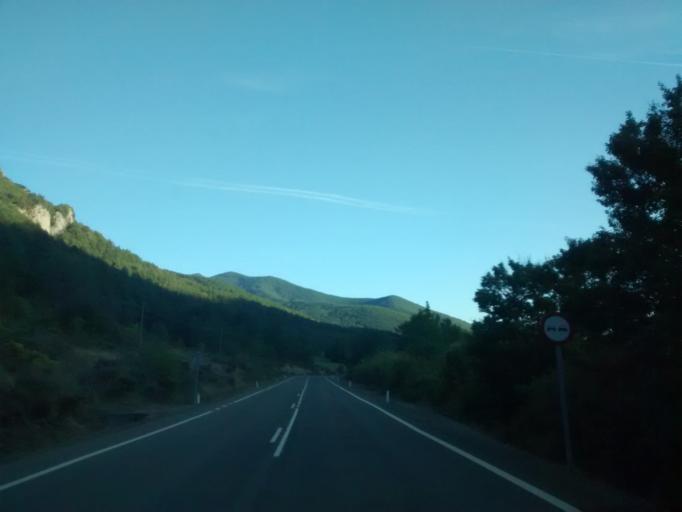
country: ES
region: Aragon
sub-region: Provincia de Huesca
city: Aragues del Puerto
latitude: 42.6916
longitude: -0.7373
